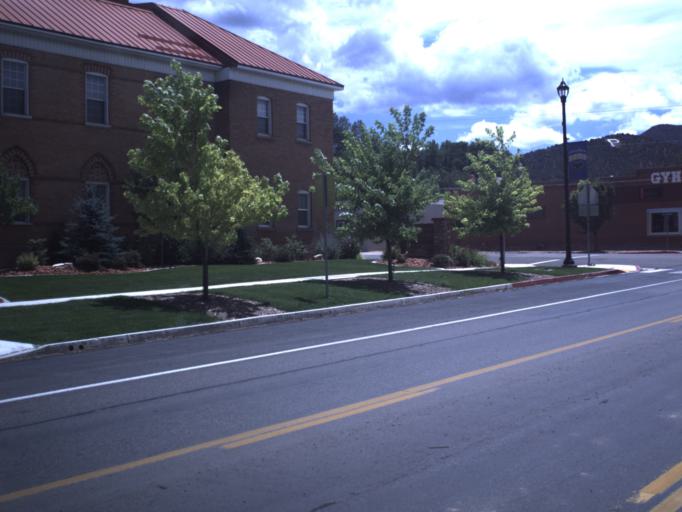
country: US
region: Utah
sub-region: Iron County
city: Parowan
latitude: 37.8447
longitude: -112.8277
